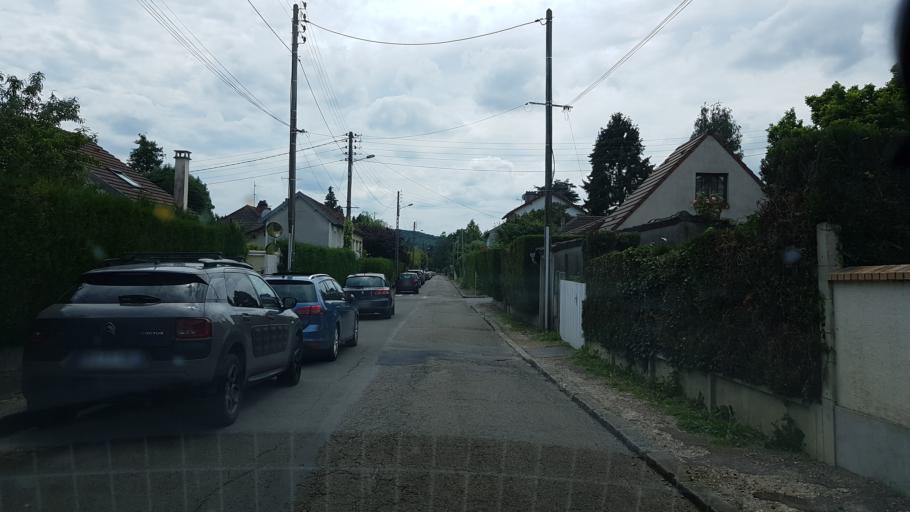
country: FR
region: Ile-de-France
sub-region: Departement des Yvelines
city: Saint-Remy-les-Chevreuse
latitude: 48.7135
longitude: 2.0679
